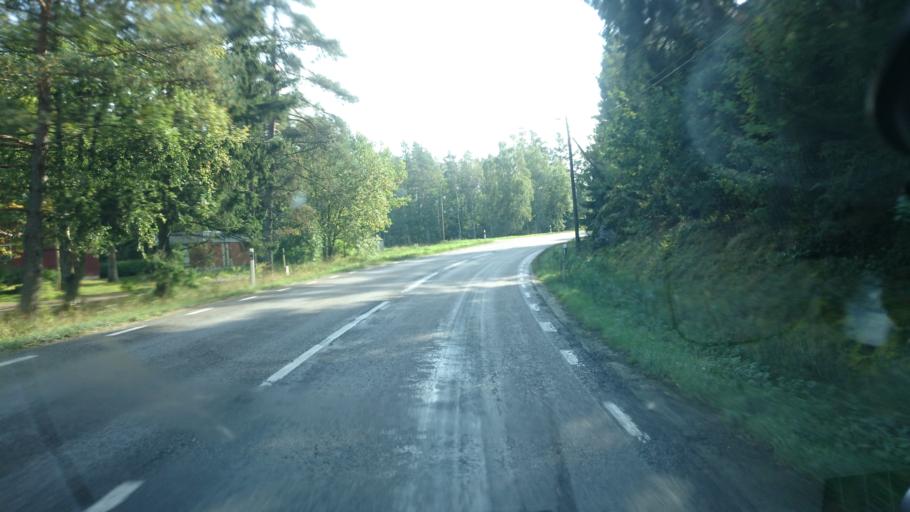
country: SE
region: Vaestra Goetaland
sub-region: Vanersborgs Kommun
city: Vargon
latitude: 58.2529
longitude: 12.4140
